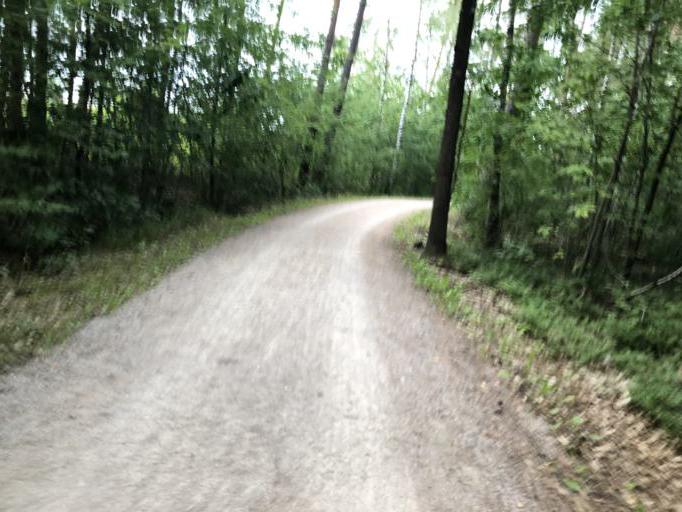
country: DE
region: Bavaria
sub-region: Regierungsbezirk Mittelfranken
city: Buckenhof
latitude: 49.5882
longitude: 11.0371
